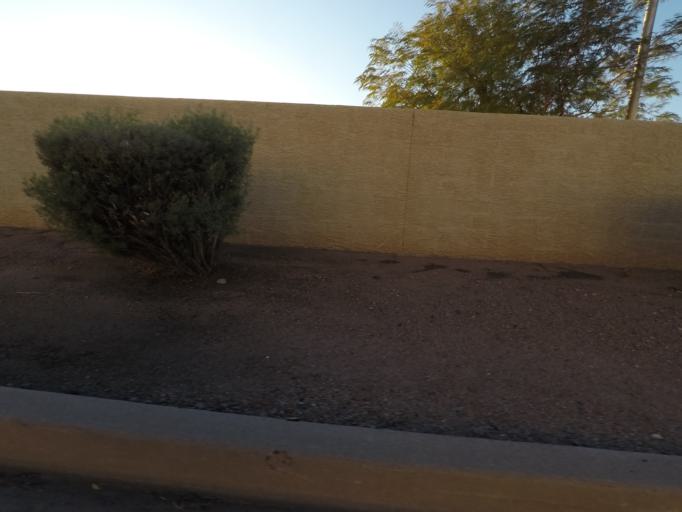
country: US
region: Arizona
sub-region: Maricopa County
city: Tempe Junction
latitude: 33.3956
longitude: -111.9479
